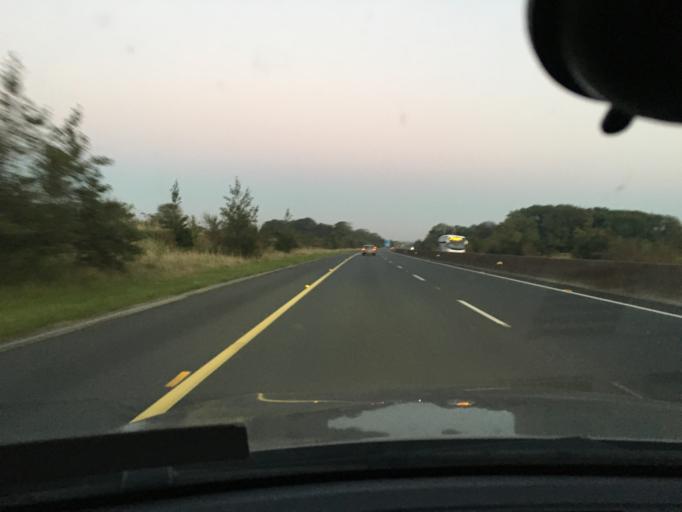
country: IE
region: Connaught
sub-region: County Galway
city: Athenry
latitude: 53.2959
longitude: -8.7882
